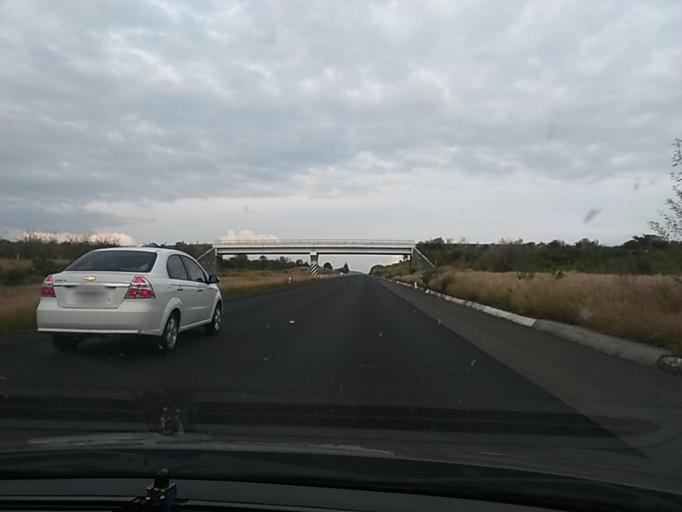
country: MX
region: Mexico
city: Huaniqueo de Morales
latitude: 19.8824
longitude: -101.4977
